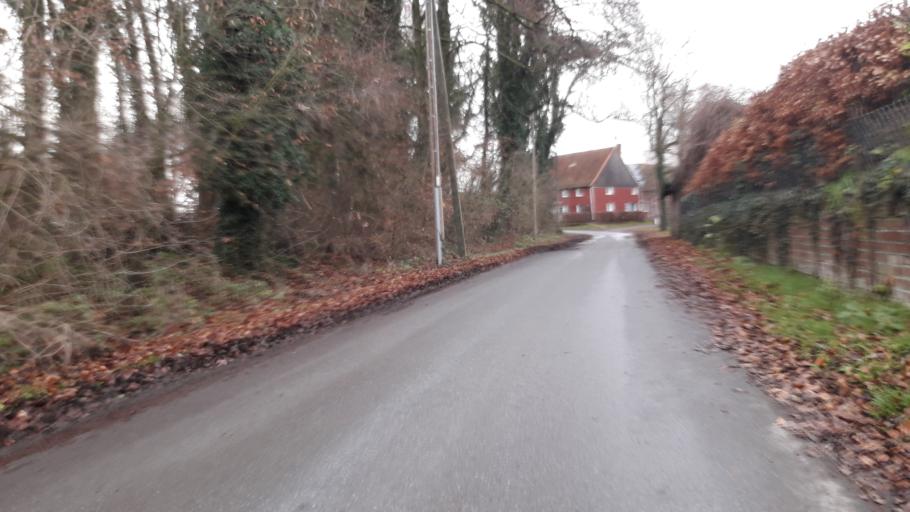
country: DE
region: North Rhine-Westphalia
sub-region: Regierungsbezirk Arnsberg
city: Welver
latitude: 51.5733
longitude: 8.0032
